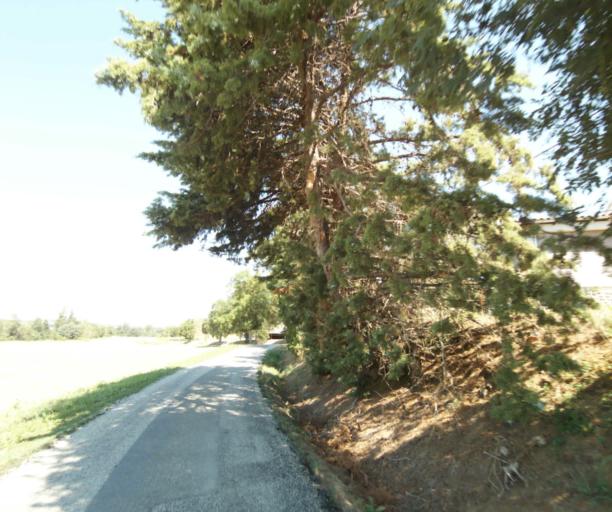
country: FR
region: Midi-Pyrenees
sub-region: Departement de l'Ariege
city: Lezat-sur-Leze
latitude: 43.2597
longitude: 1.3668
